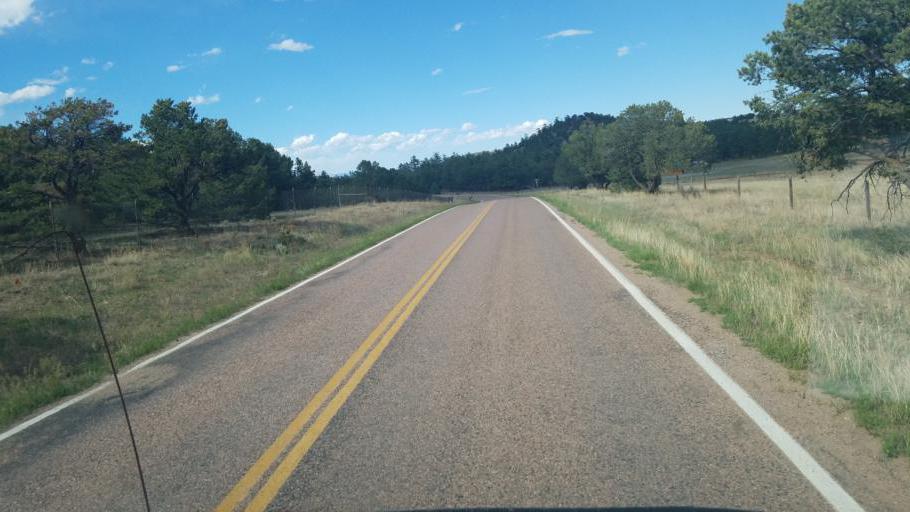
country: US
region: Colorado
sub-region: Custer County
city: Westcliffe
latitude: 38.3449
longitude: -105.4830
